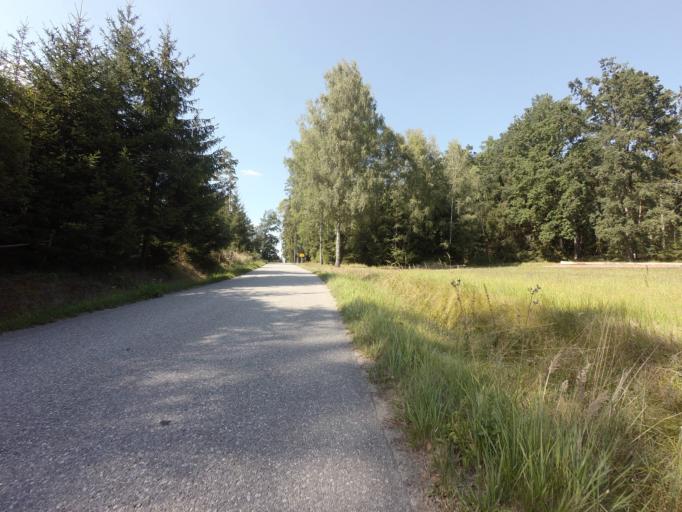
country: CZ
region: Jihocesky
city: Tyn nad Vltavou
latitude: 49.1606
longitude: 14.4296
